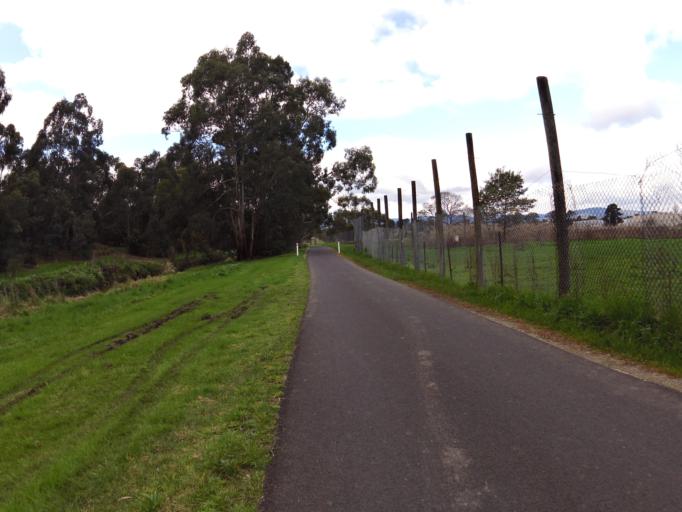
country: AU
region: Victoria
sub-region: Maroondah
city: Heathmont
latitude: -37.8389
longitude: 145.2419
